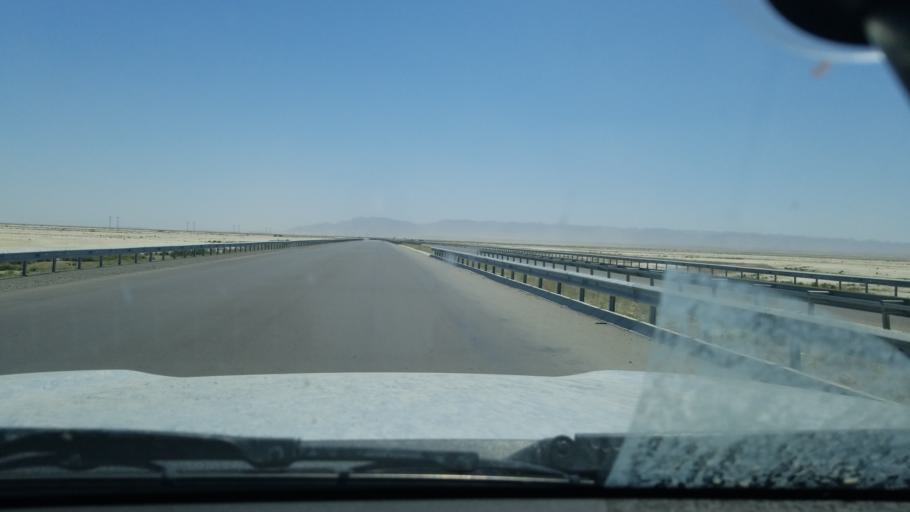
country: TM
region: Balkan
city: Gazanjyk
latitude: 39.2787
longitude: 55.2546
